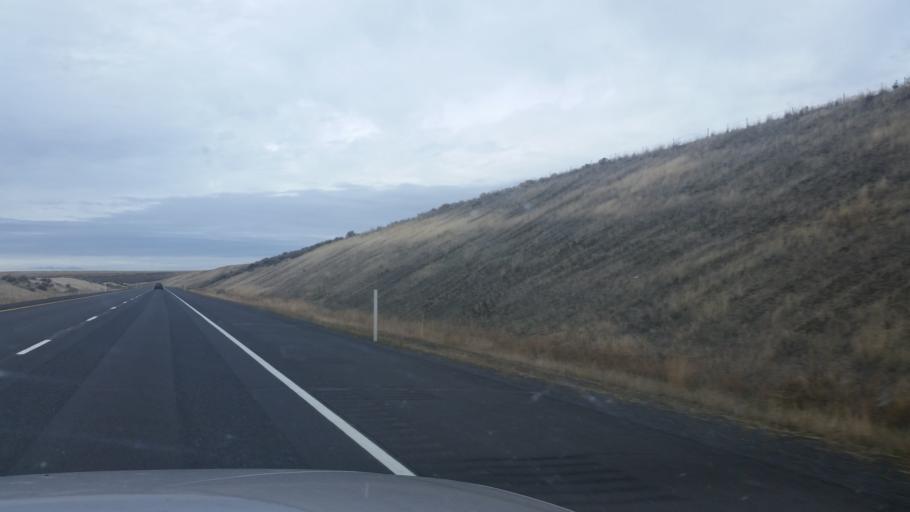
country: US
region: Washington
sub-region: Adams County
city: Ritzville
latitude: 47.1103
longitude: -118.5579
